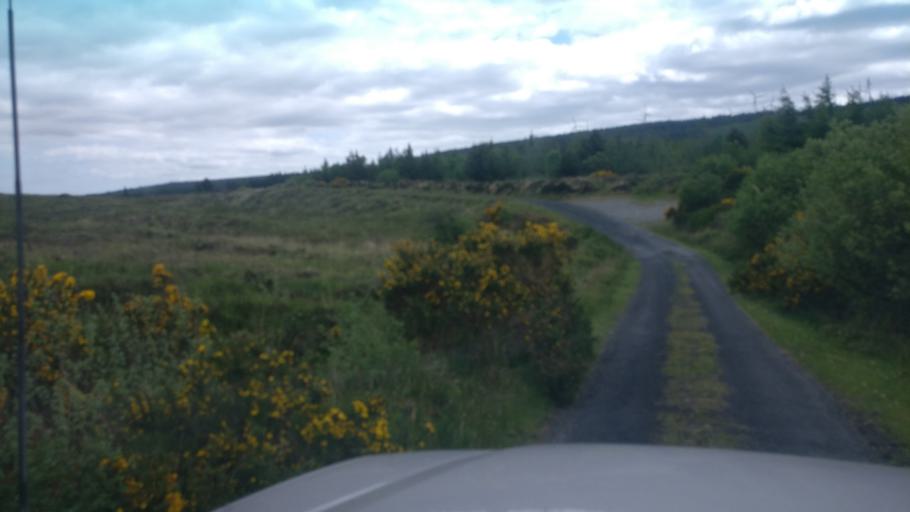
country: IE
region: Connaught
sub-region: County Galway
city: Loughrea
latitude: 53.1125
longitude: -8.6292
